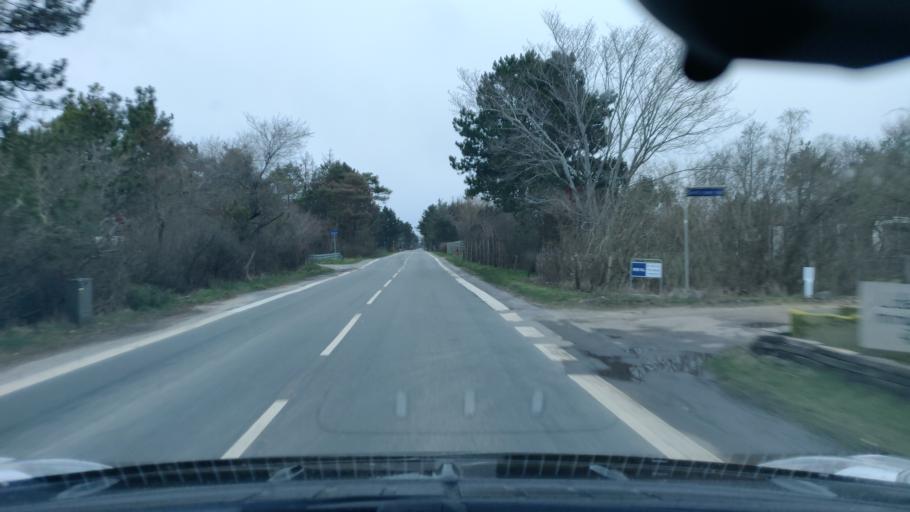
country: DK
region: Zealand
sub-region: Odsherred Kommune
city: Asnaes
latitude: 55.8693
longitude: 11.5381
